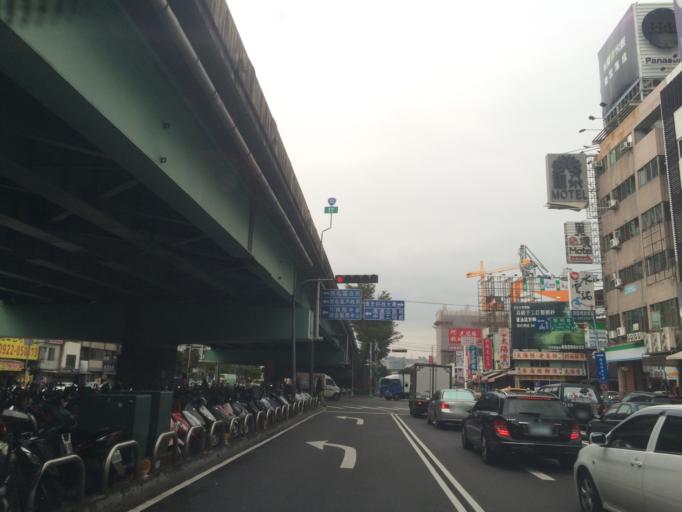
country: TW
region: Taiwan
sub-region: Taichung City
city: Taichung
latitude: 24.1708
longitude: 120.6370
